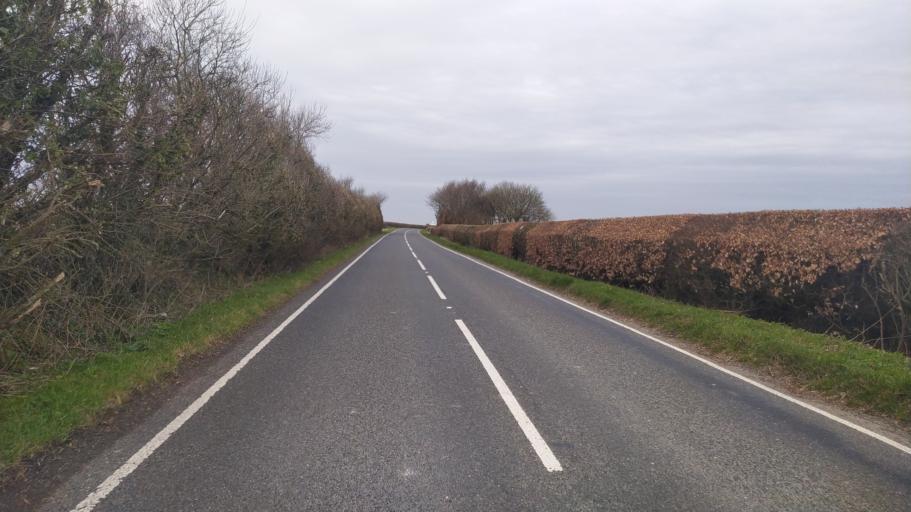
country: GB
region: England
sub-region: Dorset
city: Beaminster
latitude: 50.8394
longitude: -2.7056
